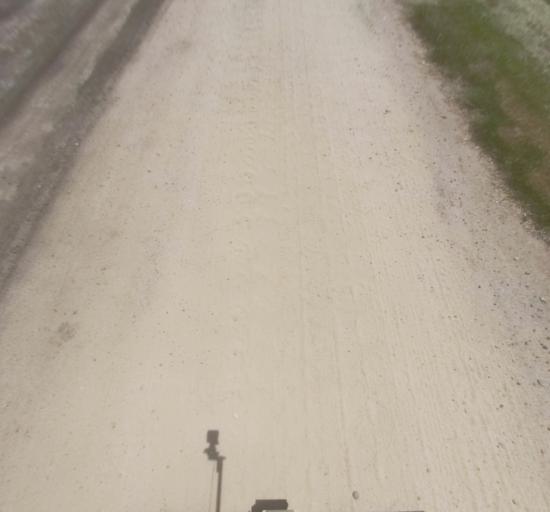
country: US
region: California
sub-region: Madera County
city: Chowchilla
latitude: 37.0034
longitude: -120.3483
